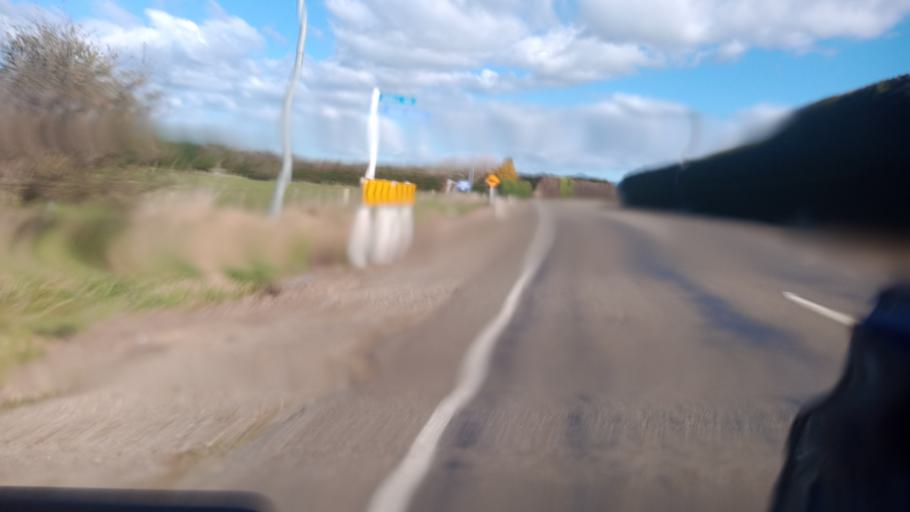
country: NZ
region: Bay of Plenty
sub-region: Opotiki District
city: Opotiki
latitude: -37.9990
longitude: 177.2981
